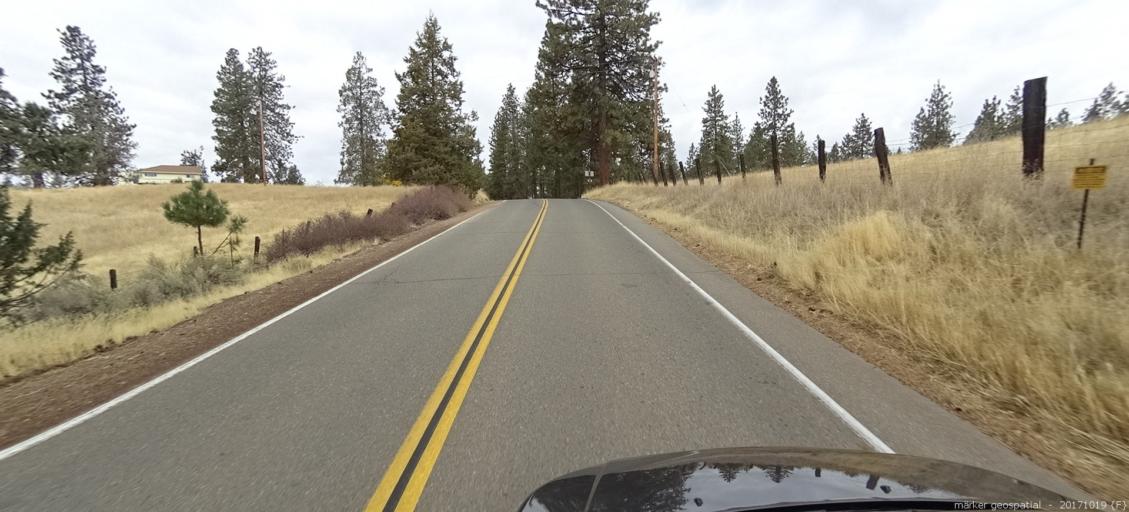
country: US
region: California
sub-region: Shasta County
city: Burney
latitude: 41.0563
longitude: -121.3677
